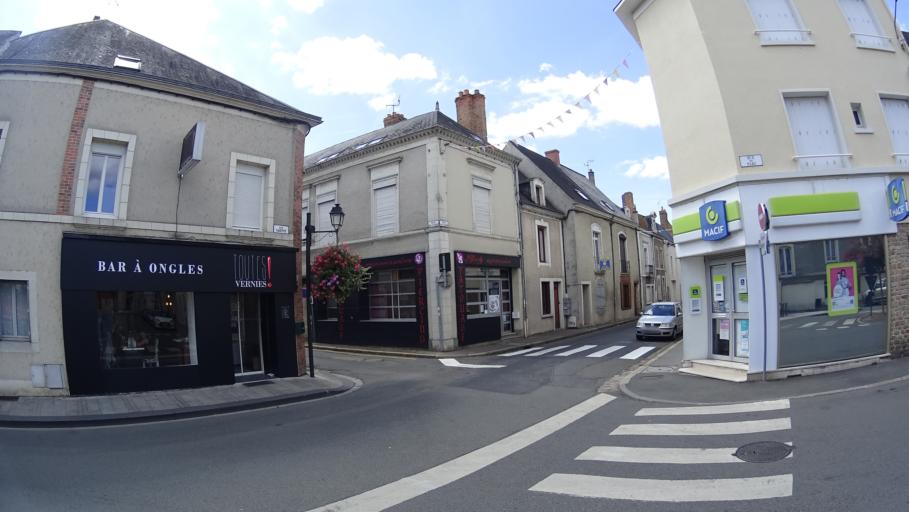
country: FR
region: Pays de la Loire
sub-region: Departement de la Sarthe
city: La Fleche
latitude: 47.6996
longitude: -0.0789
